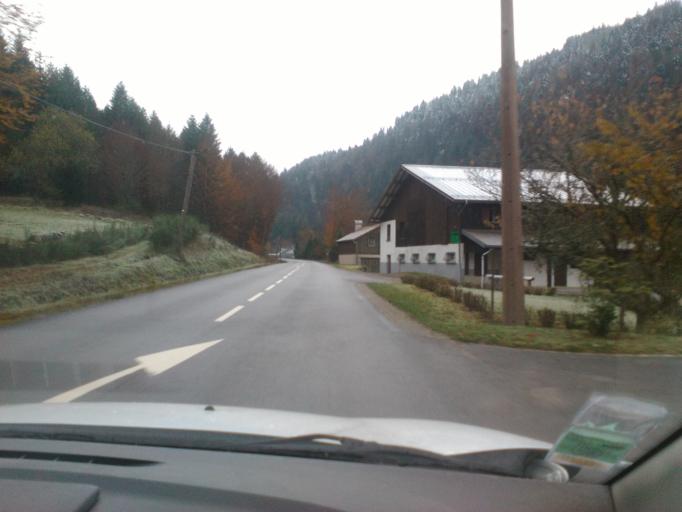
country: FR
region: Lorraine
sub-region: Departement des Vosges
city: Xonrupt-Longemer
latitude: 48.0644
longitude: 6.9622
